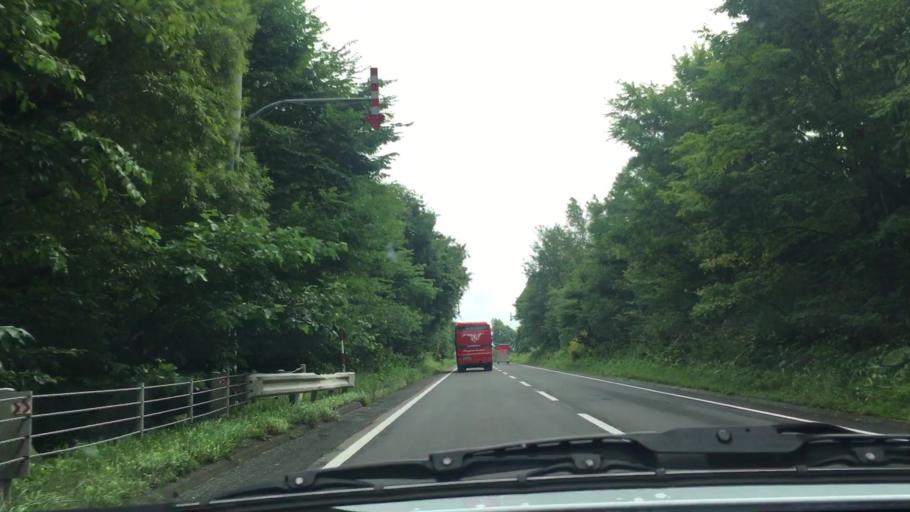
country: JP
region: Hokkaido
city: Chitose
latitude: 42.9431
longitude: 141.7527
